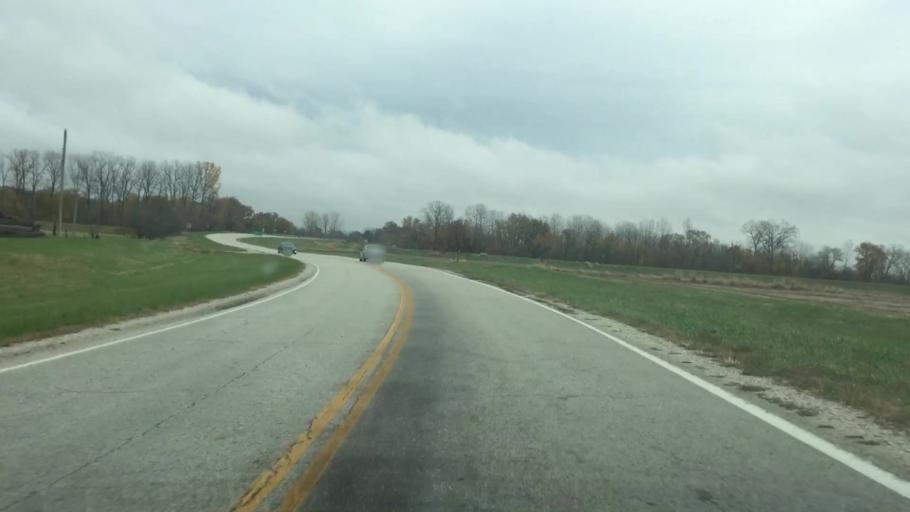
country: US
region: Missouri
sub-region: Gasconade County
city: Hermann
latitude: 38.7278
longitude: -91.4525
